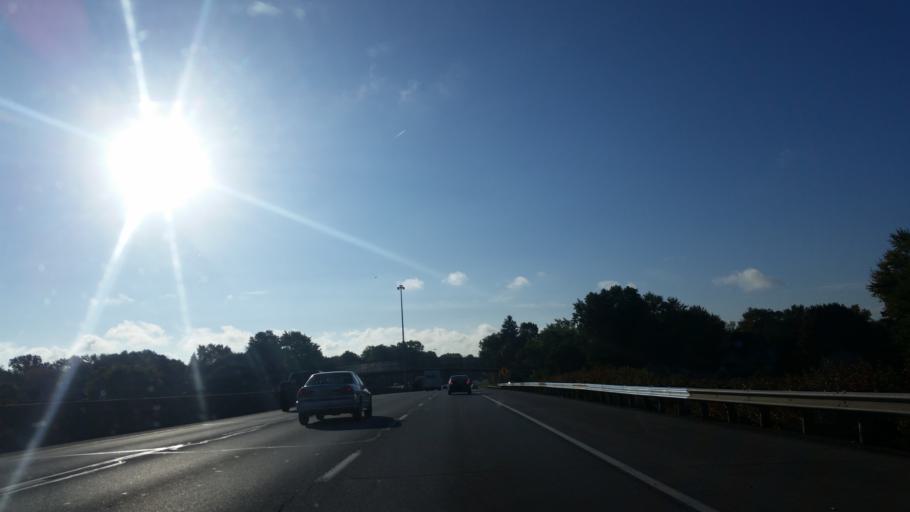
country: US
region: Ohio
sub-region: Summit County
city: Fairlawn
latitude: 41.0834
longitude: -81.5787
